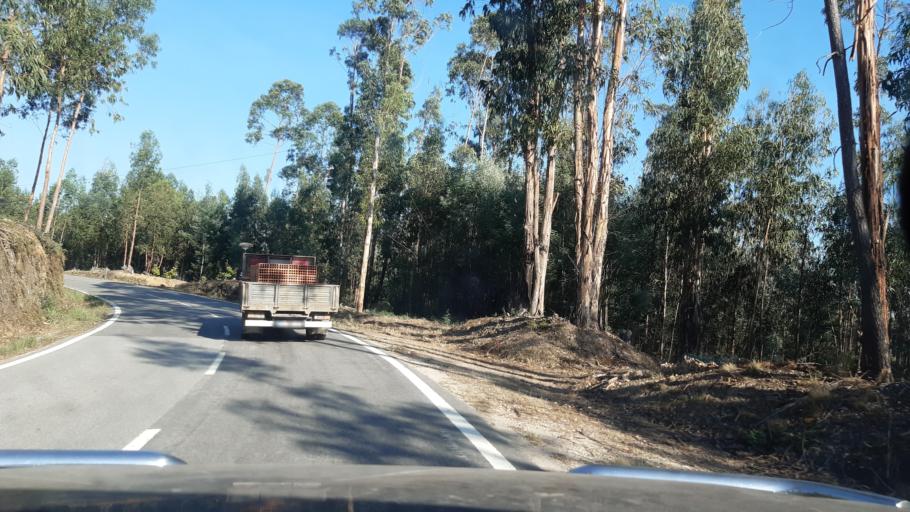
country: PT
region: Aveiro
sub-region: Agueda
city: Aguada de Cima
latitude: 40.5638
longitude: -8.3759
